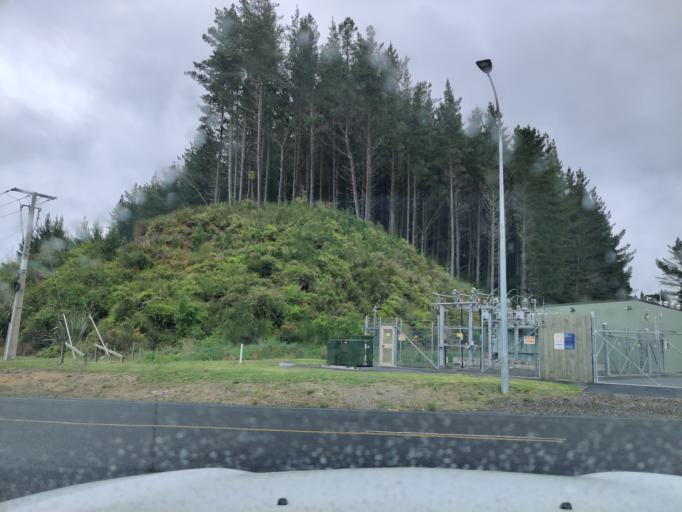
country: NZ
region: Bay of Plenty
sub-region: Rotorua District
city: Rotorua
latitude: -38.1764
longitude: 176.2533
